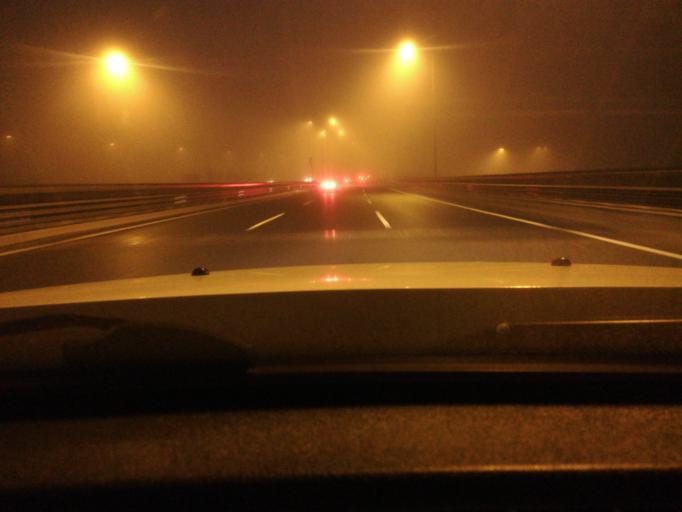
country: TR
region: Istanbul
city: Sultanbeyli
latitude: 40.9655
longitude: 29.3213
